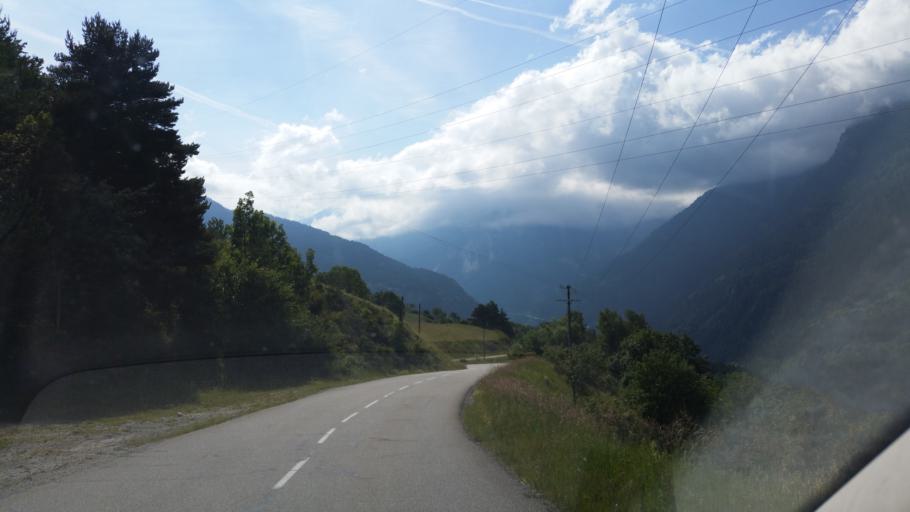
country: FR
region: Rhone-Alpes
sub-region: Departement de la Savoie
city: Modane
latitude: 45.2078
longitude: 6.6002
